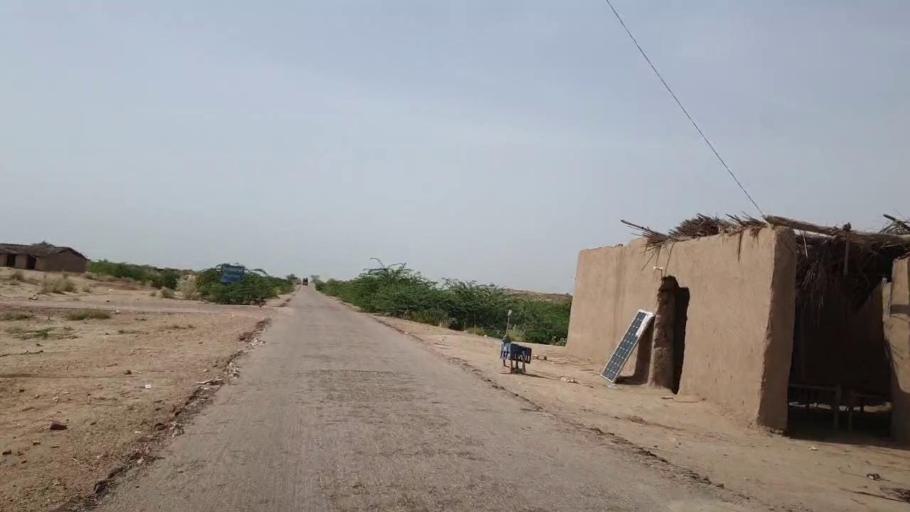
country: PK
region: Sindh
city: Bandhi
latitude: 26.5541
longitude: 68.3834
